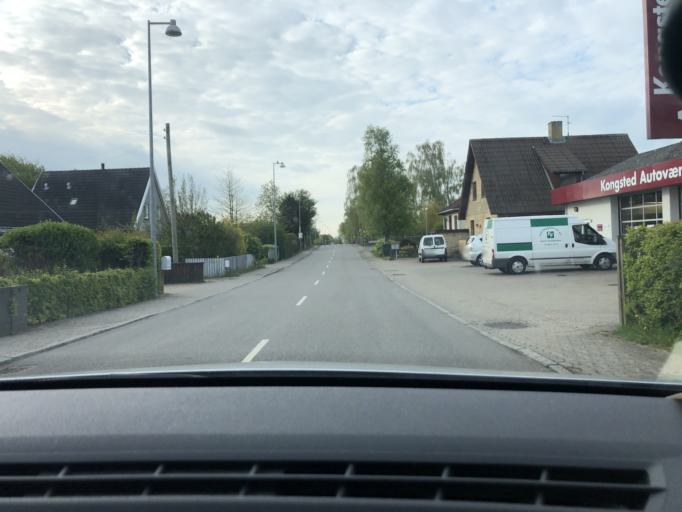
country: DK
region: Zealand
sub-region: Faxe Kommune
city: Ronnede
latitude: 55.2428
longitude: 12.0425
